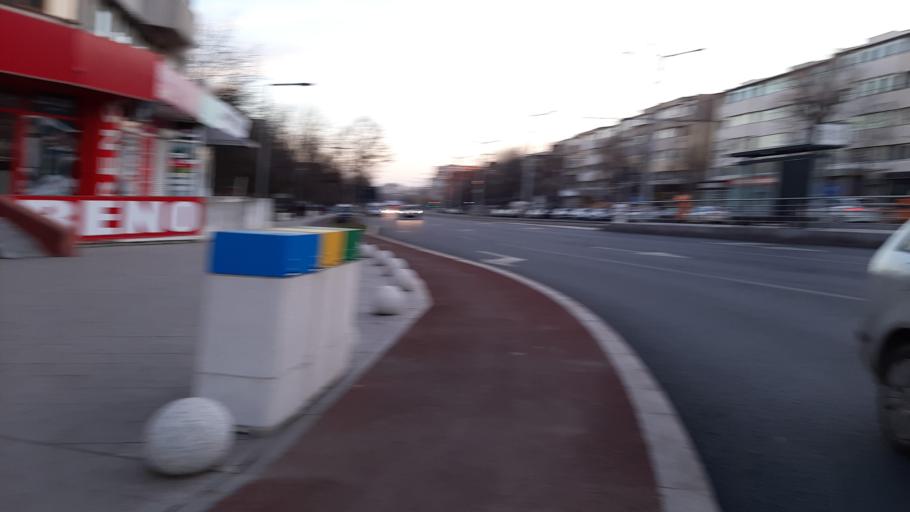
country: RO
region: Galati
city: Galati
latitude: 45.4338
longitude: 28.0256
